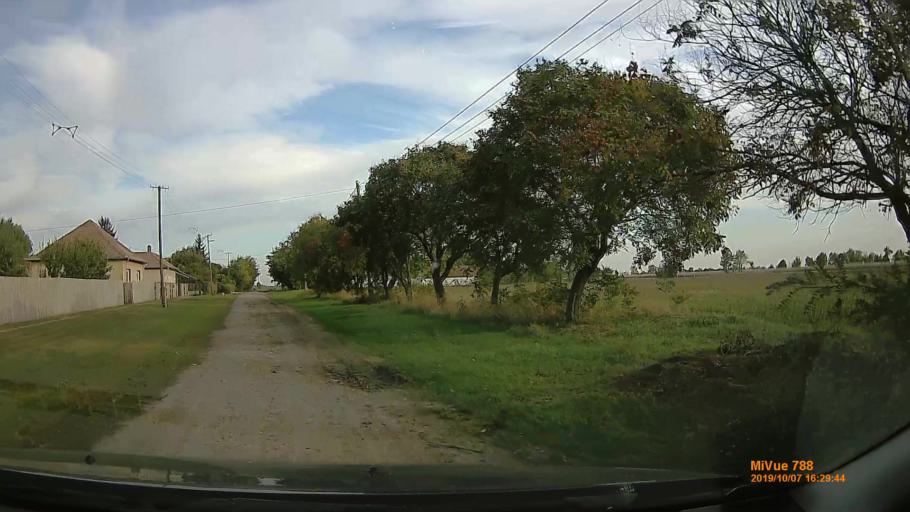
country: HU
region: Bekes
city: Szarvas
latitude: 46.8186
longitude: 20.6522
